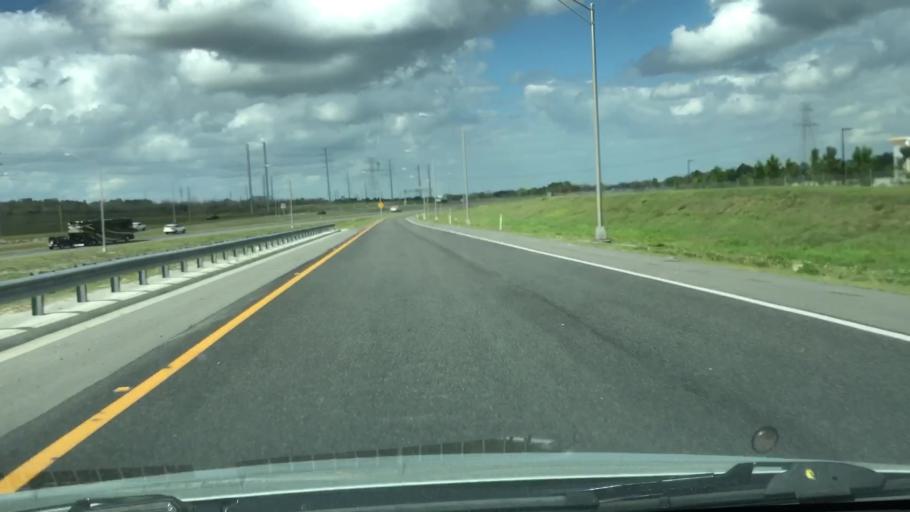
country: US
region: Florida
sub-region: Orange County
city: Oakland
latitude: 28.4760
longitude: -81.6304
